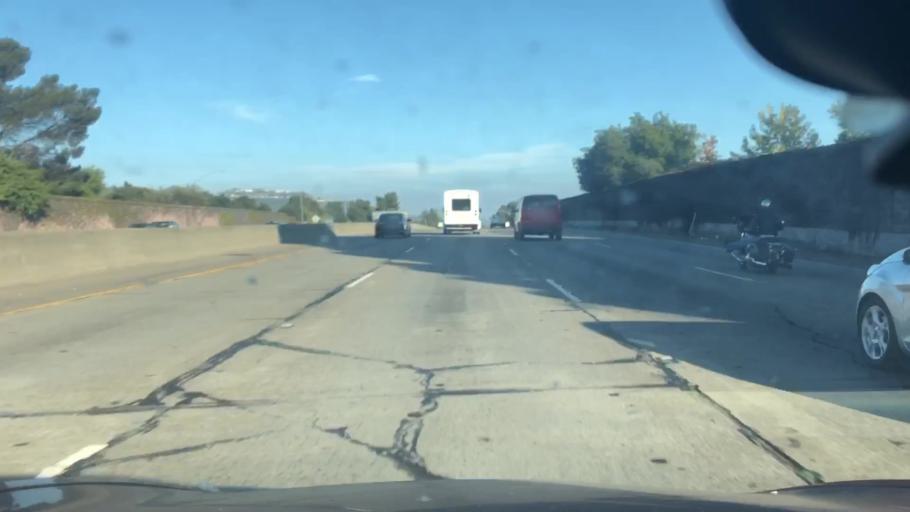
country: US
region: California
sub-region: Alameda County
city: Piedmont
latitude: 37.7964
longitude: -122.2104
